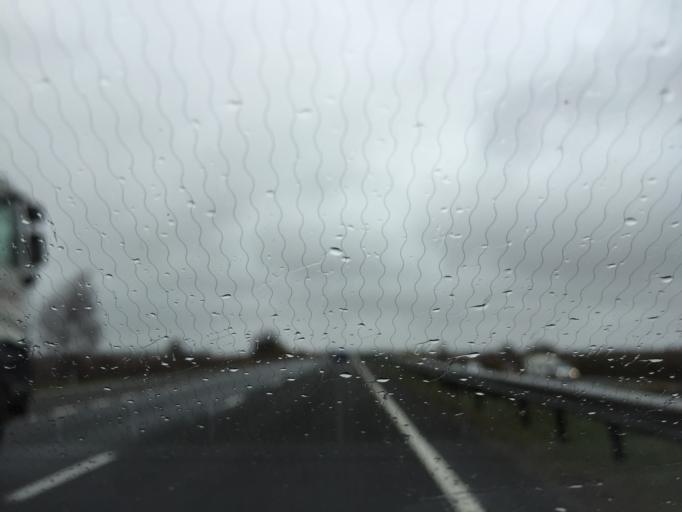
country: GB
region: England
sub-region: Hampshire
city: Ringwood
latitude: 50.8563
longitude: -1.7260
